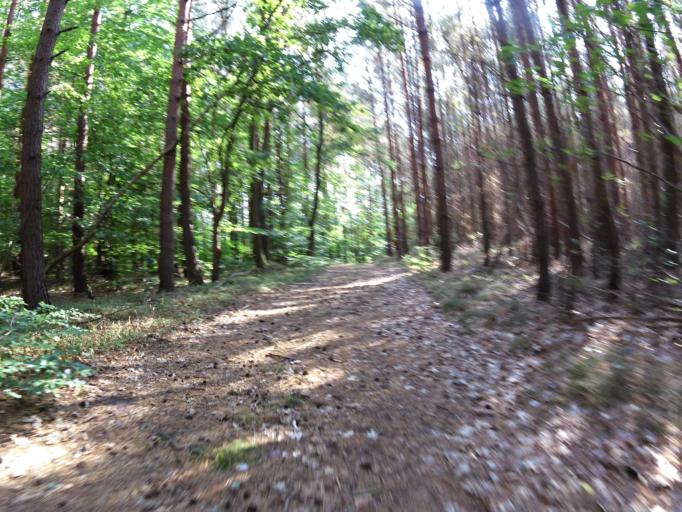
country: DE
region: Mecklenburg-Vorpommern
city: Loddin
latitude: 54.0081
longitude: 14.0552
